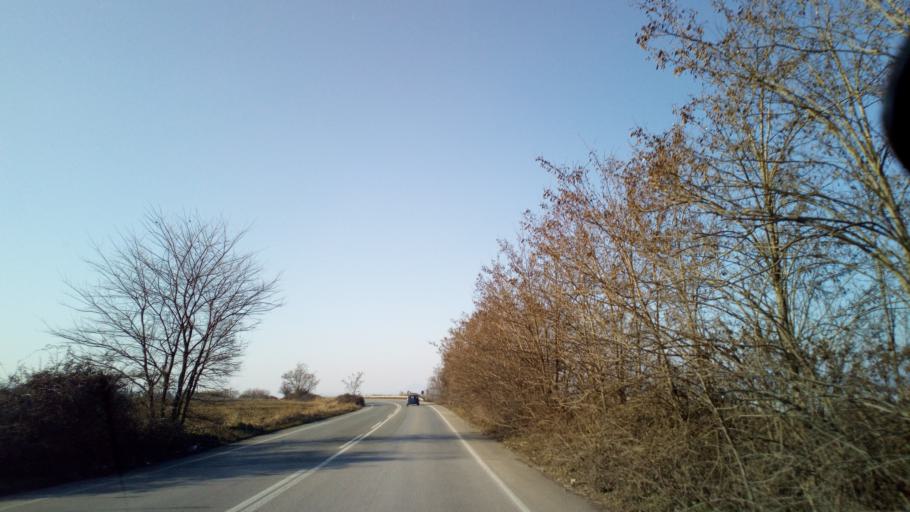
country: GR
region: Central Macedonia
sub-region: Nomos Thessalonikis
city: Gerakarou
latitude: 40.6470
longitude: 23.1770
